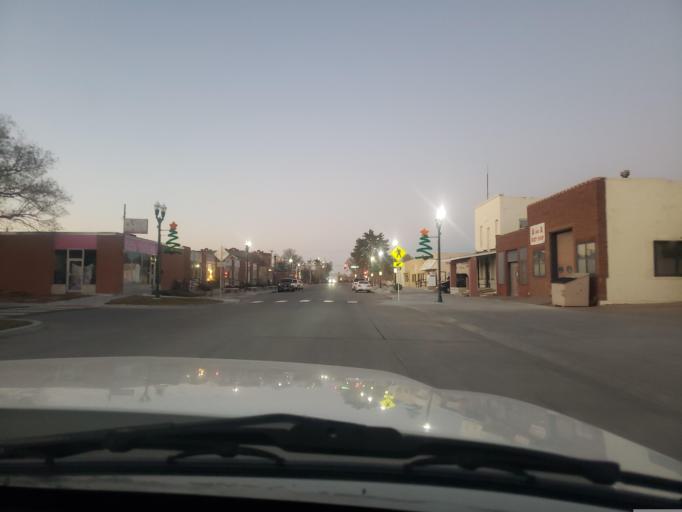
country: US
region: Kansas
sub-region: Finney County
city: Garden City
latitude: 37.9707
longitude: -100.8751
